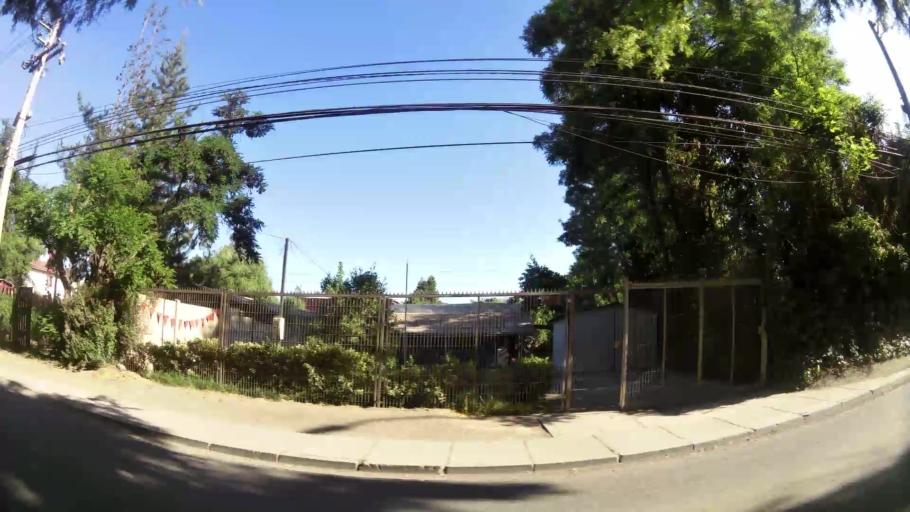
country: CL
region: Santiago Metropolitan
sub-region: Provincia de Maipo
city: San Bernardo
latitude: -33.6390
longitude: -70.6827
